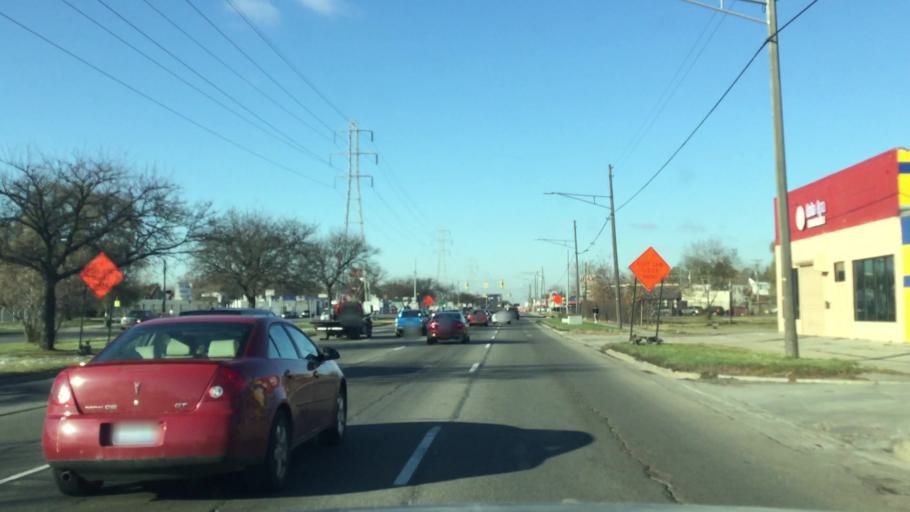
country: US
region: Michigan
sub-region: Macomb County
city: Warren
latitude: 42.4477
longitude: -83.0600
